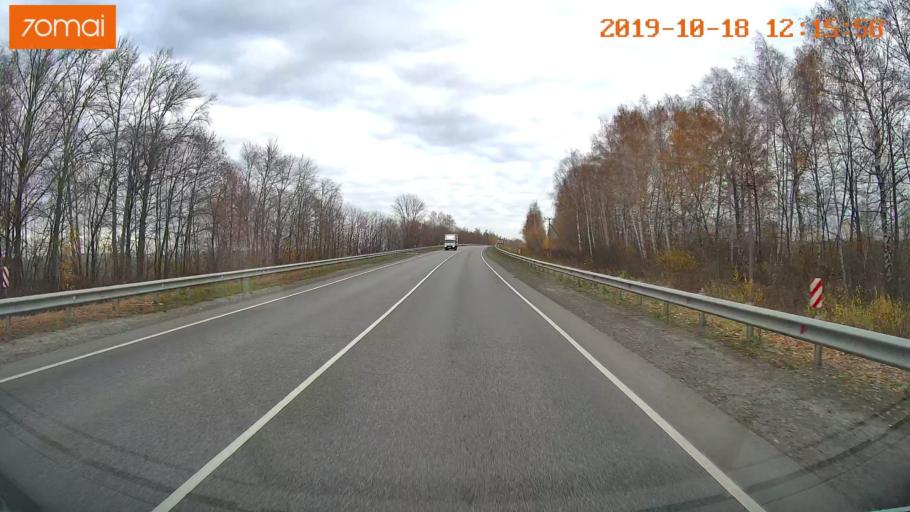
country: RU
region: Rjazan
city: Zakharovo
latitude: 54.4491
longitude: 39.4103
